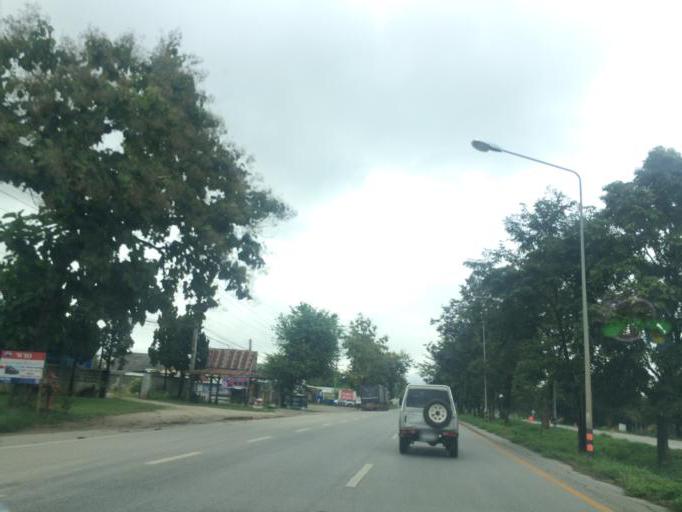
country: TH
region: Chiang Rai
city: Mae Lao
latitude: 19.7575
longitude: 99.7333
